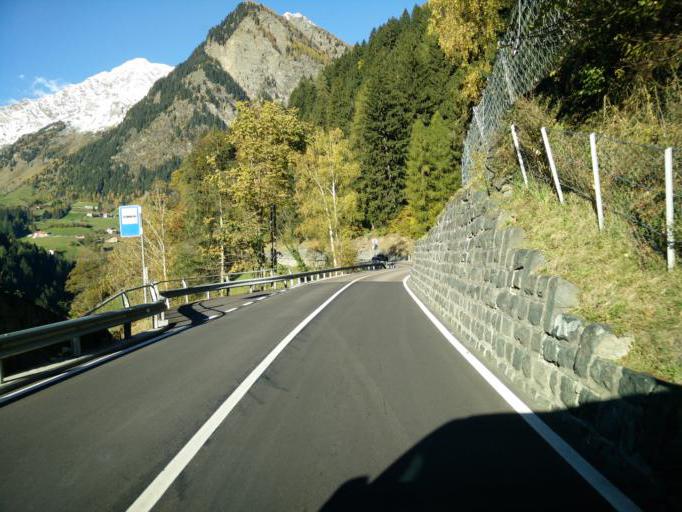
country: IT
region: Trentino-Alto Adige
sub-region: Bolzano
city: Moso in Passiria
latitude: 46.8274
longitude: 11.1774
